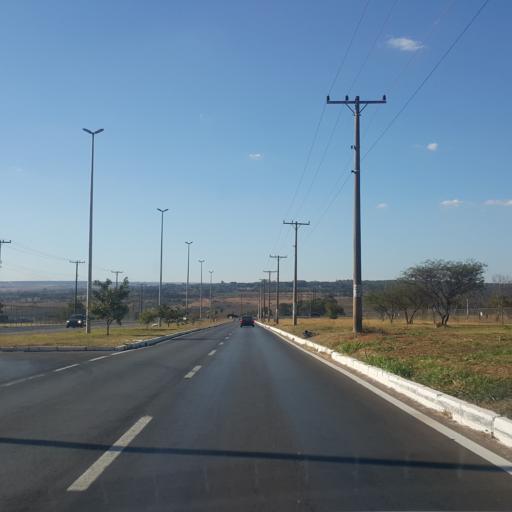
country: BR
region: Federal District
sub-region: Brasilia
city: Brasilia
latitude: -15.7893
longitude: -48.1176
